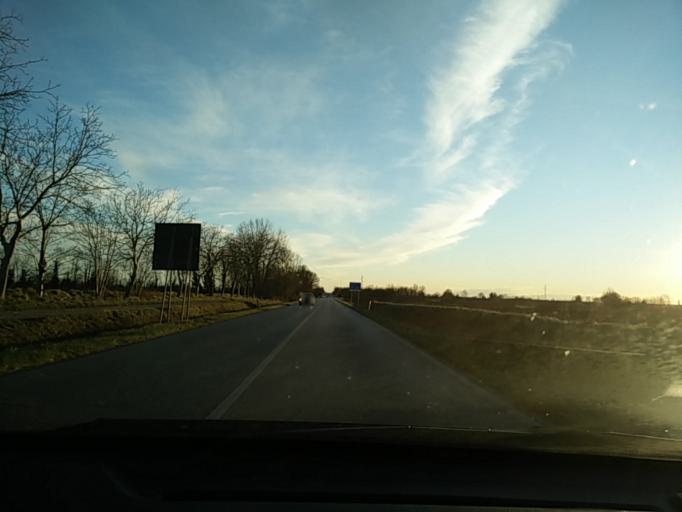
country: IT
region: Friuli Venezia Giulia
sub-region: Provincia di Udine
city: Bertiolo
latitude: 45.9516
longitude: 13.0922
